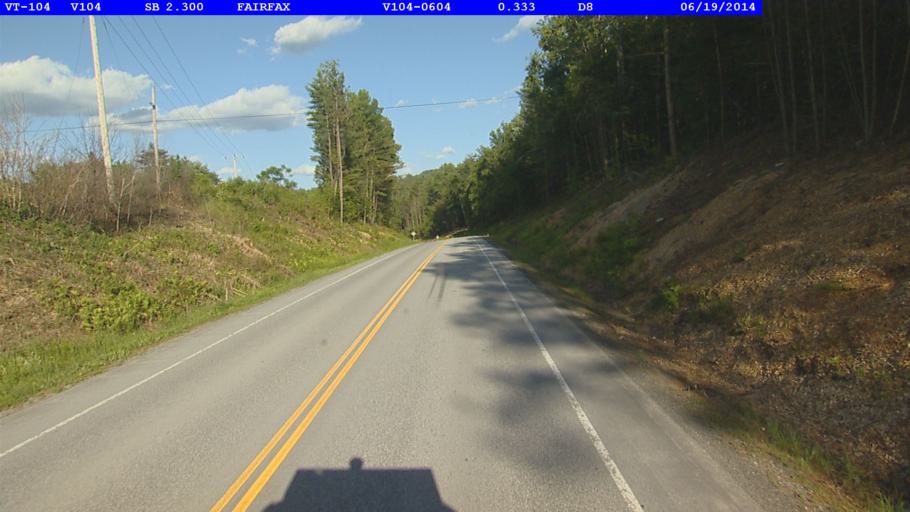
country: US
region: Vermont
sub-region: Chittenden County
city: Jericho
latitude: 44.6389
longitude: -72.9319
